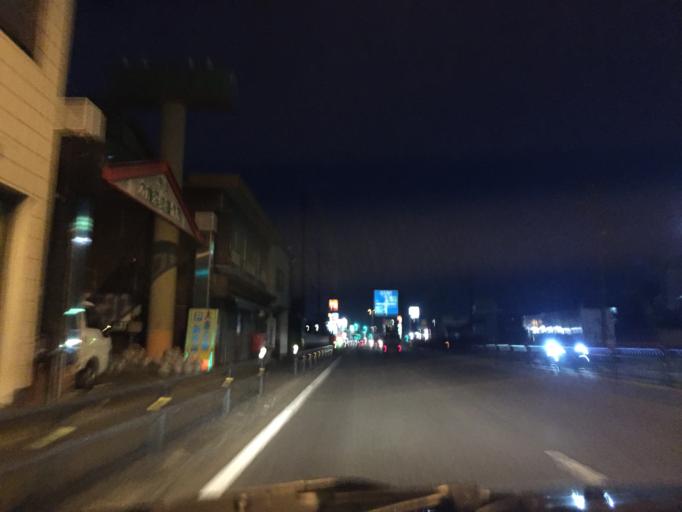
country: JP
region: Gifu
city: Ogaki
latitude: 35.3209
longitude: 136.6188
